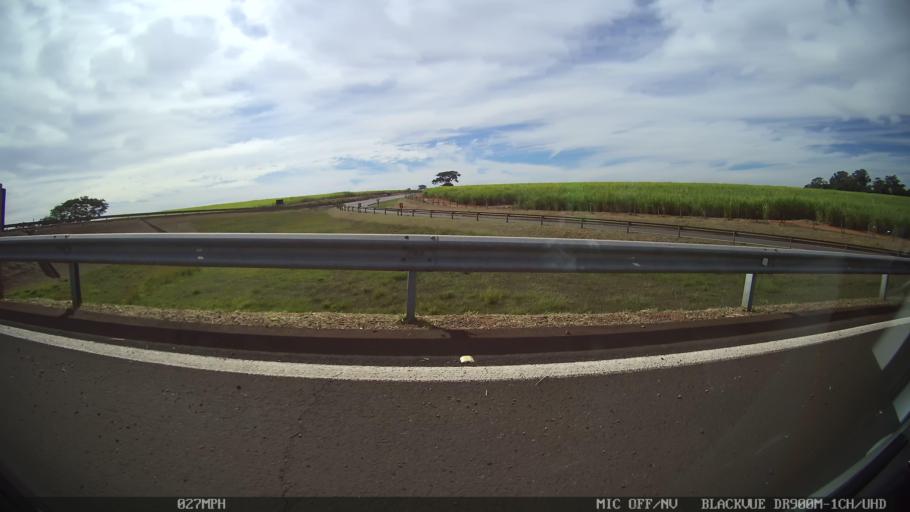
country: BR
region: Sao Paulo
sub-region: Taquaritinga
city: Taquaritinga
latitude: -21.5150
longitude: -48.5399
